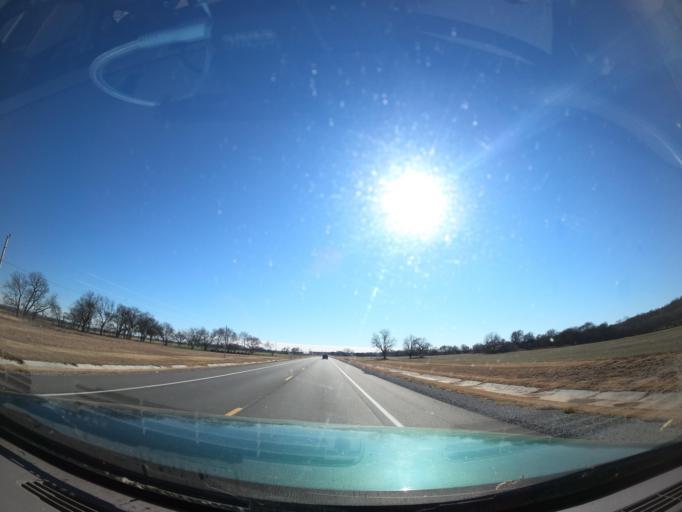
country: US
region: Oklahoma
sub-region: Wagoner County
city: Coweta
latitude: 35.8947
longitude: -95.6592
